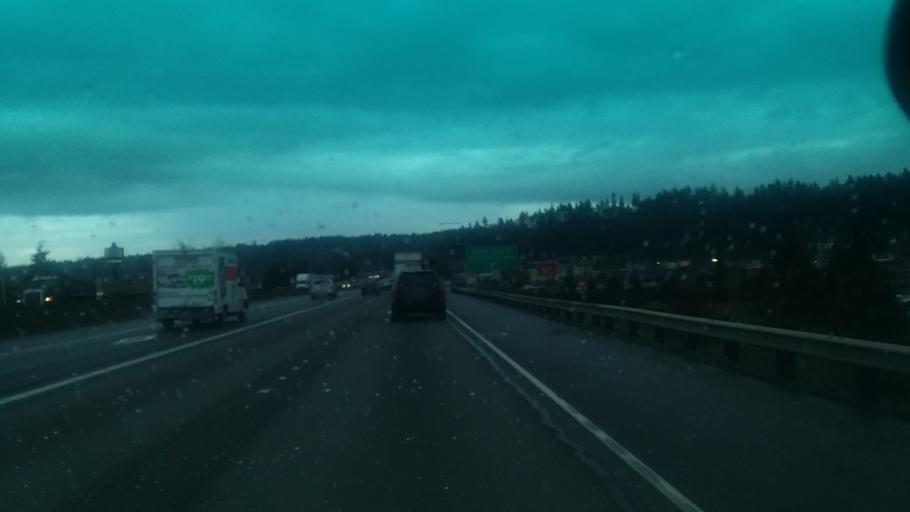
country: US
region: Washington
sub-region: King County
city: Kent
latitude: 47.3957
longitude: -122.2312
